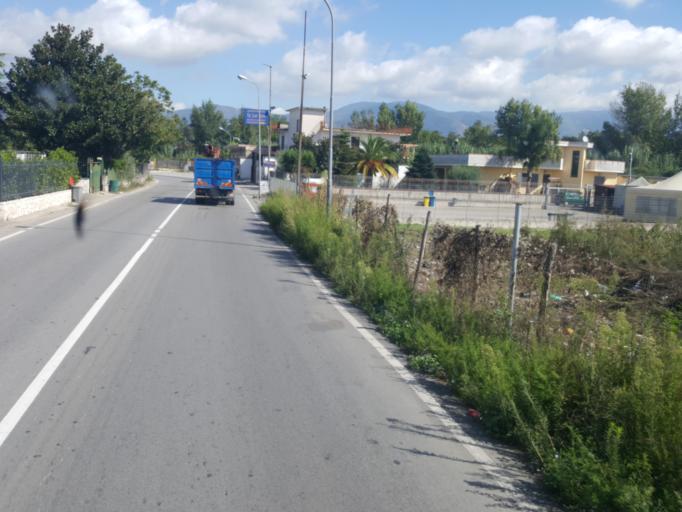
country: IT
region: Campania
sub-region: Provincia di Napoli
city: Nola
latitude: 40.9290
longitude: 14.5106
